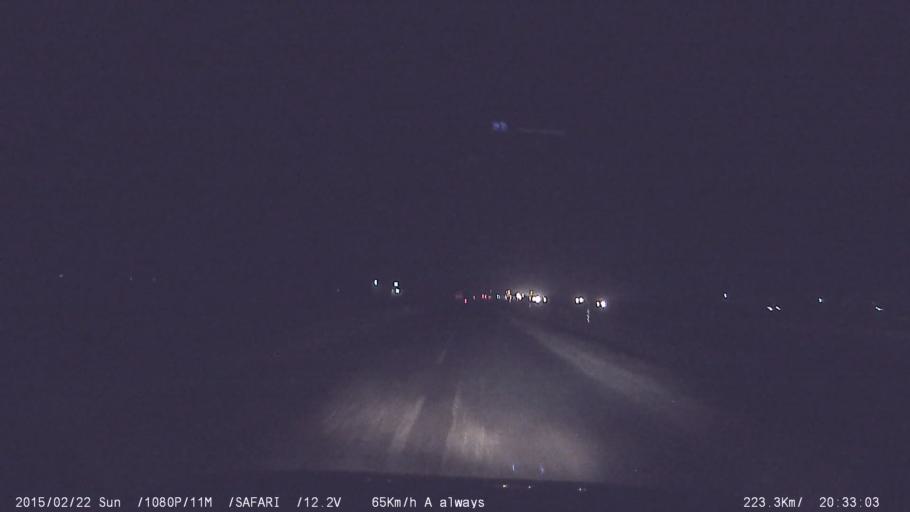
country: IN
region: Tamil Nadu
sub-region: Dindigul
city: Dindigul
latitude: 10.3536
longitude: 77.9493
